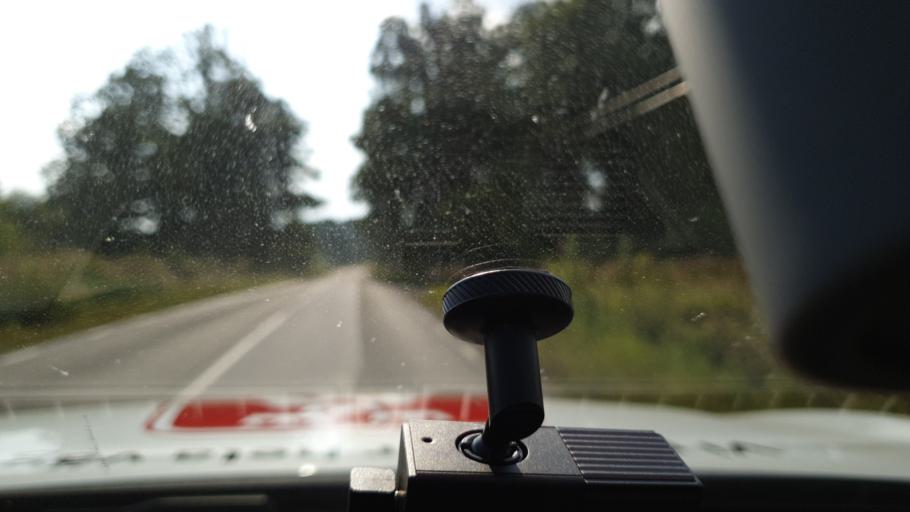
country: SE
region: Kalmar
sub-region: Vimmerby Kommun
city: Sodra Vi
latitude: 57.7309
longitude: 15.8352
